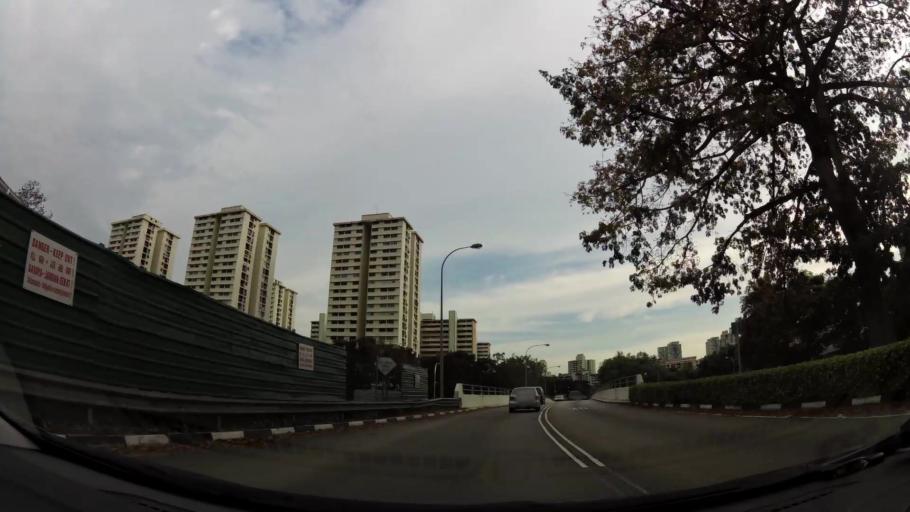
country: SG
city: Singapore
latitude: 1.3439
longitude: 103.8537
